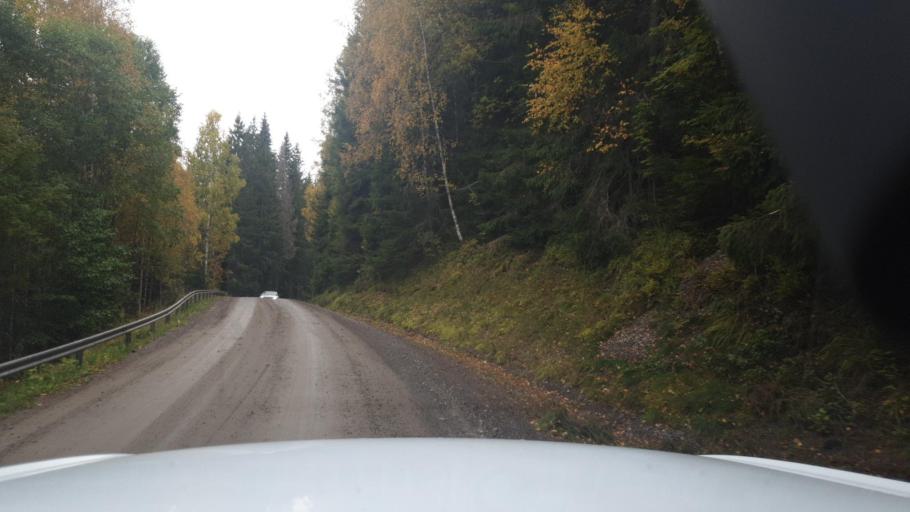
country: SE
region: Vaermland
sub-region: Eda Kommun
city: Charlottenberg
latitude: 60.0290
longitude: 12.6063
